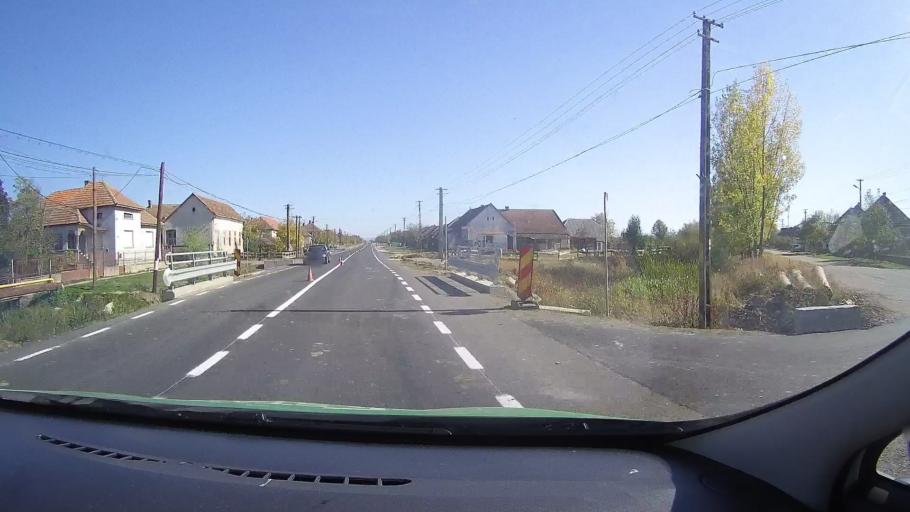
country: RO
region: Satu Mare
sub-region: Oras Ardud
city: Madaras
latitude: 47.6840
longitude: 22.8615
